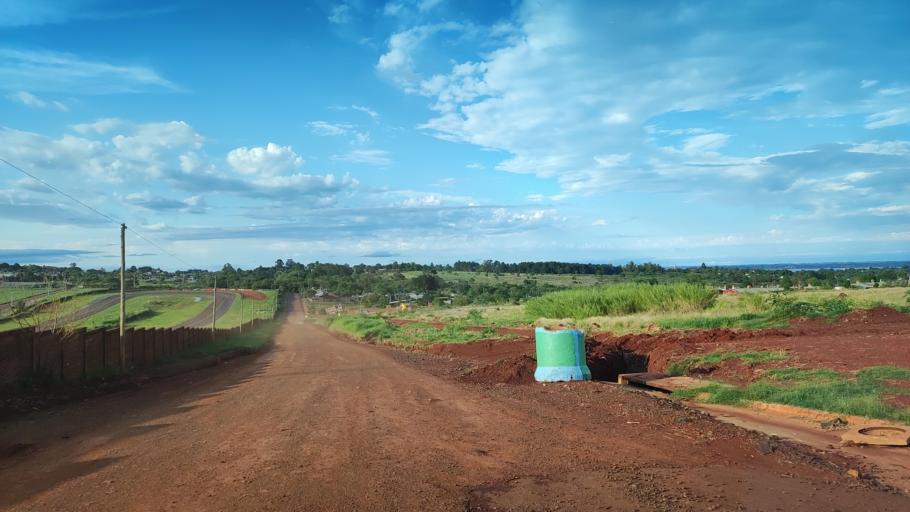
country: AR
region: Misiones
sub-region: Departamento de Capital
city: Posadas
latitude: -27.4402
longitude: -55.9244
